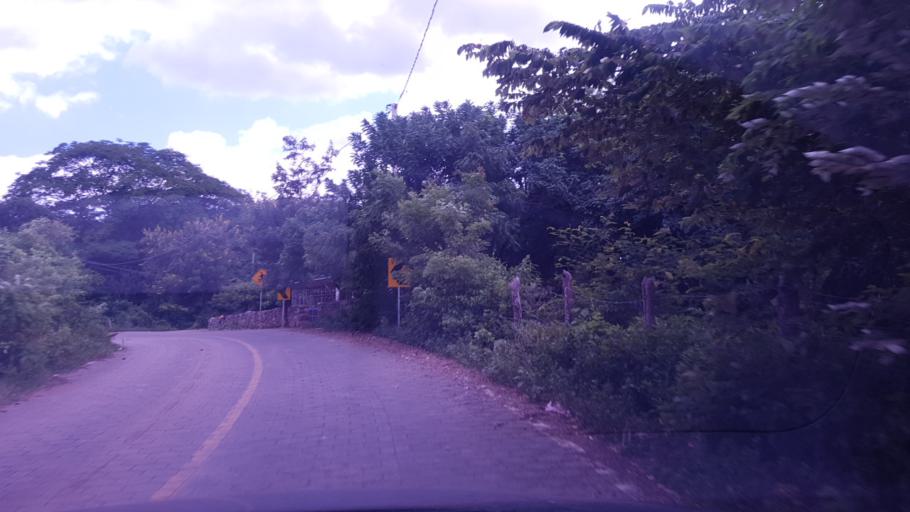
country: NI
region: Rivas
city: Tola
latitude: 11.3922
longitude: -86.0293
